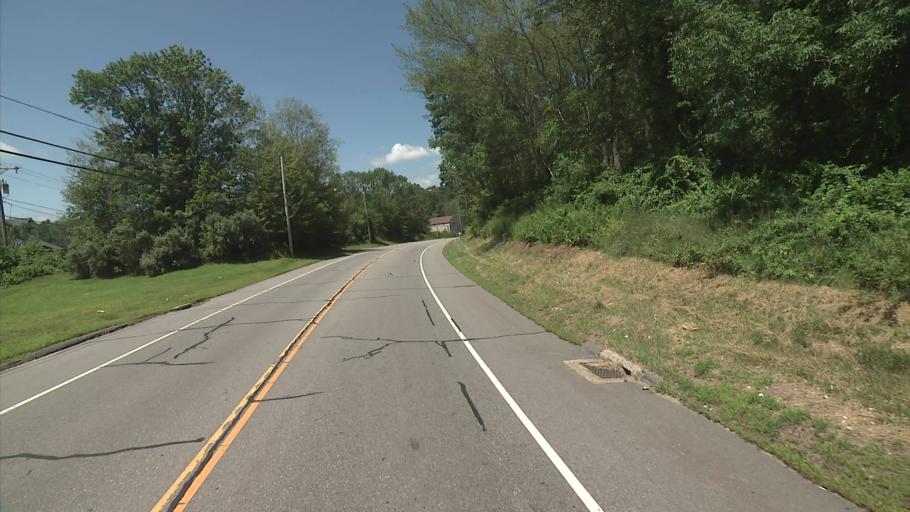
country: US
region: Connecticut
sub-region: Windham County
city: Plainfield Village
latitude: 41.6975
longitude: -71.9981
